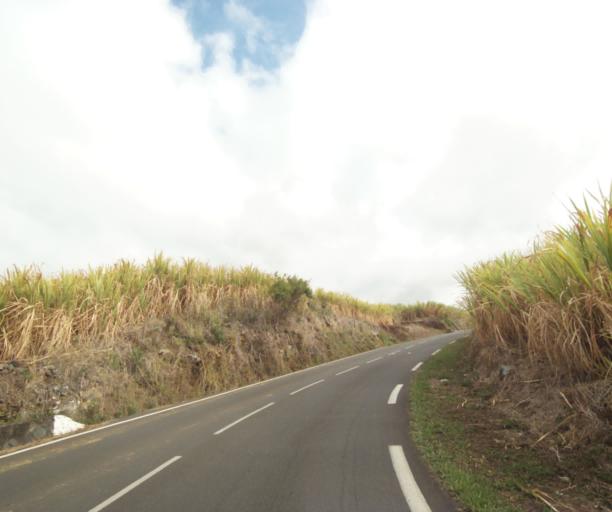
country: RE
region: Reunion
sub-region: Reunion
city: Saint-Paul
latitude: -21.0240
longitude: 55.3144
